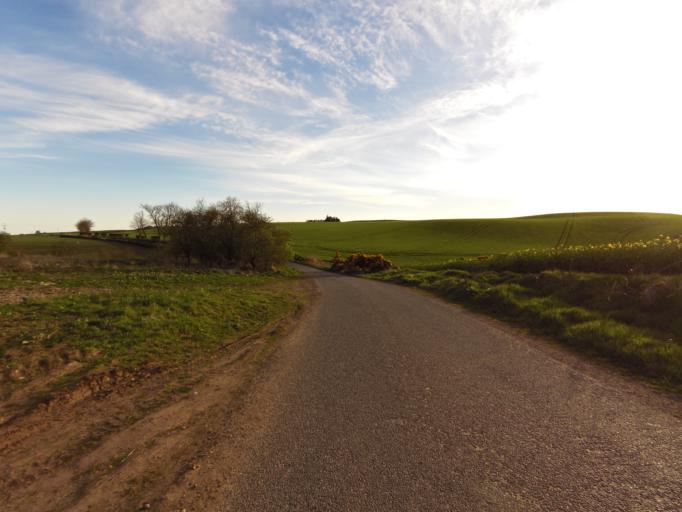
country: GB
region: Scotland
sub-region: Aberdeenshire
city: Inverbervie
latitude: 56.8895
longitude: -2.2374
